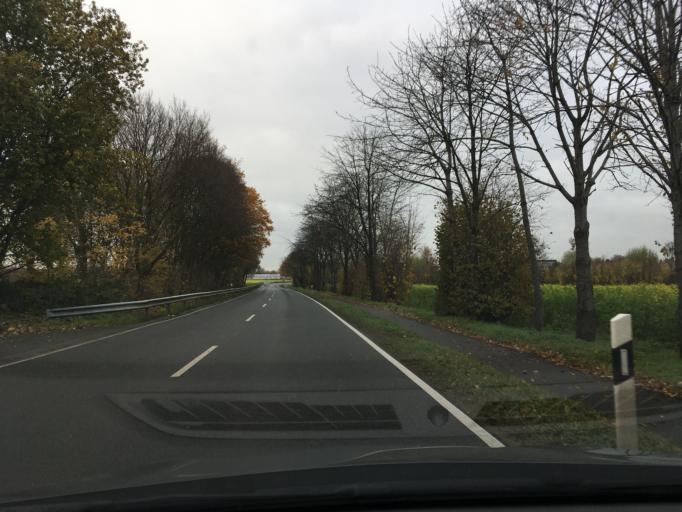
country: DE
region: North Rhine-Westphalia
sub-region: Regierungsbezirk Munster
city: Ahaus
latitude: 52.0831
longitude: 6.9710
